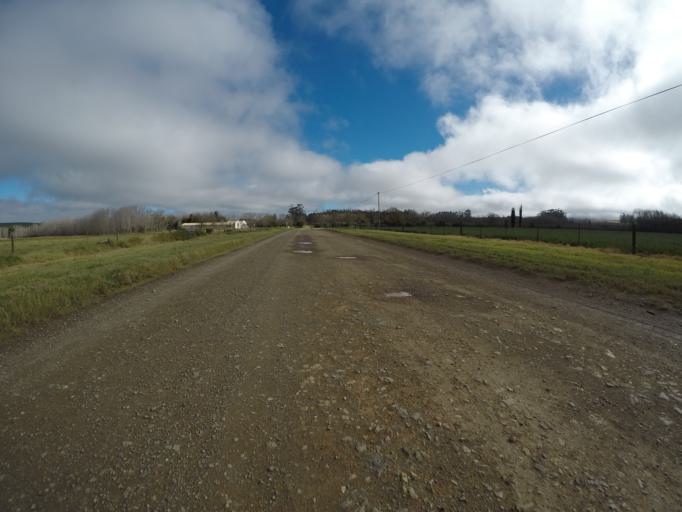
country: ZA
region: Western Cape
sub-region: Cape Winelands District Municipality
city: Ashton
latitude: -34.1260
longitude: 19.8170
